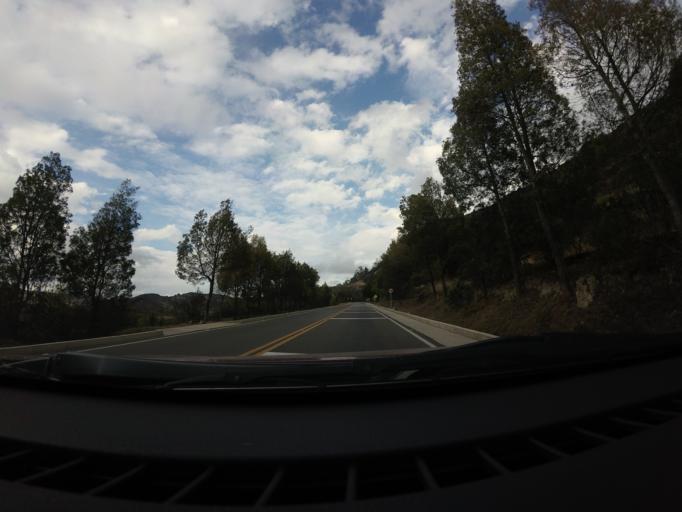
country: CO
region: Boyaca
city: Cucaita
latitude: 5.5503
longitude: -73.4357
